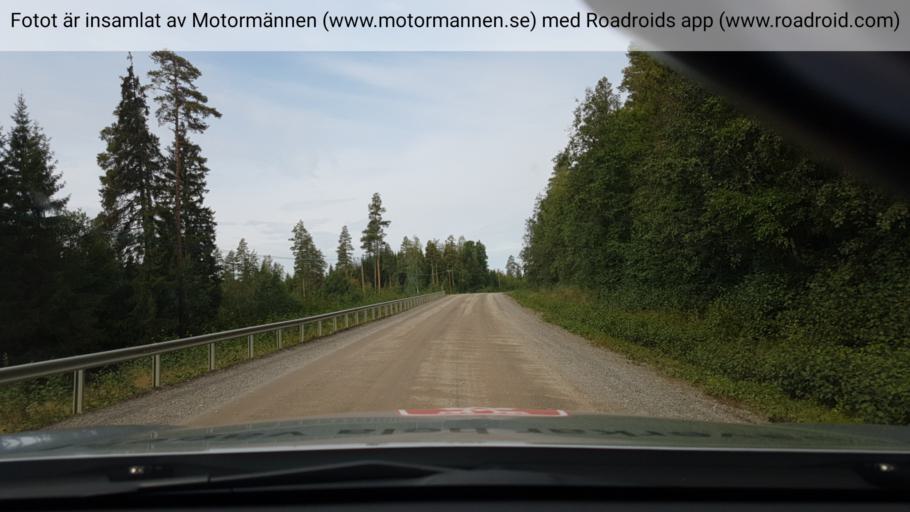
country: SE
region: Vaesterbotten
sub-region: Bjurholms Kommun
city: Bjurholm
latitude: 63.9190
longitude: 19.3766
